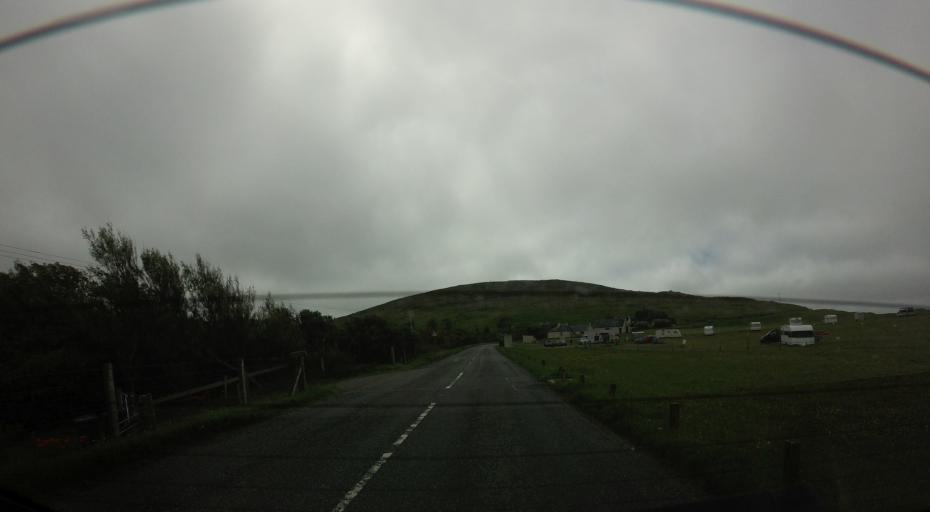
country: GB
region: Scotland
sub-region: Eilean Siar
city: Harris
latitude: 57.8624
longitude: -6.9767
